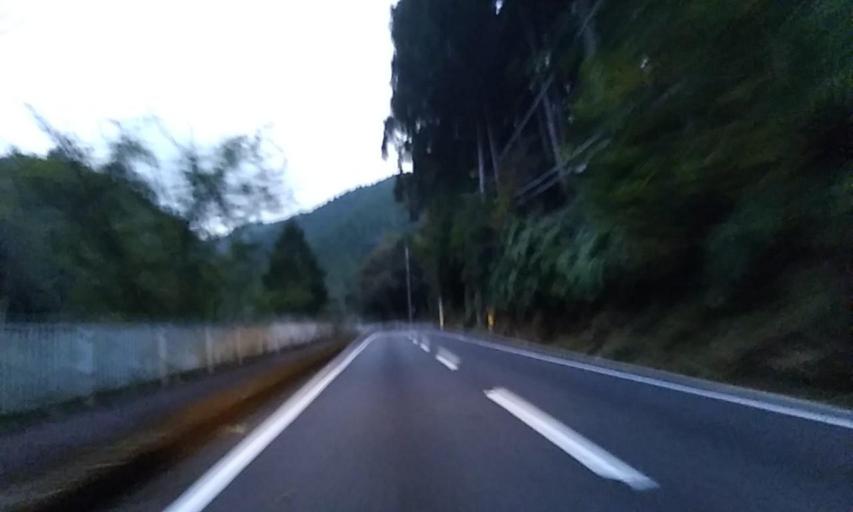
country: JP
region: Wakayama
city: Shingu
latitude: 33.7346
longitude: 135.9306
